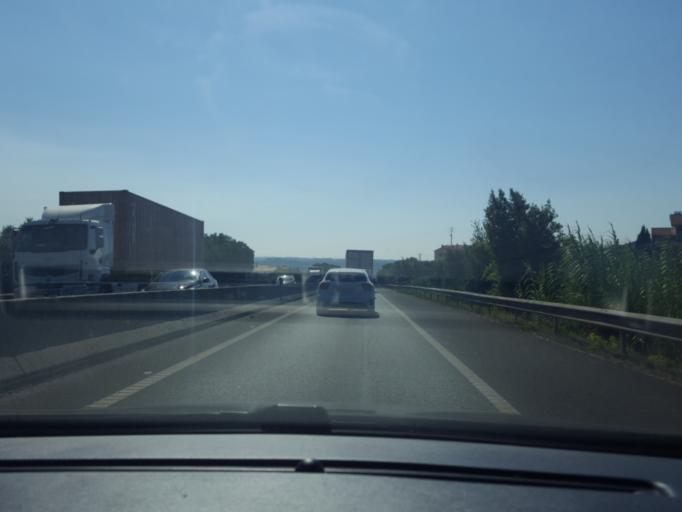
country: PT
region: Leiria
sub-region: Leiria
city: Leiria
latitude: 39.7597
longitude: -8.8074
